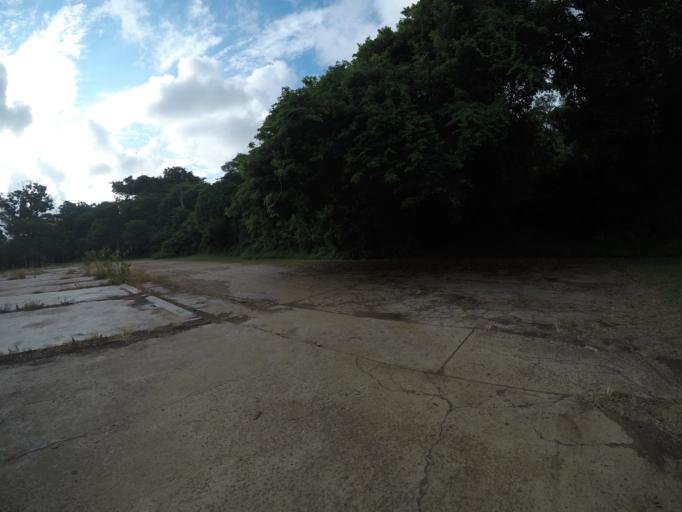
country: ZA
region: KwaZulu-Natal
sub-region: uMkhanyakude District Municipality
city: Mtubatuba
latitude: -28.3883
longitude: 32.4082
